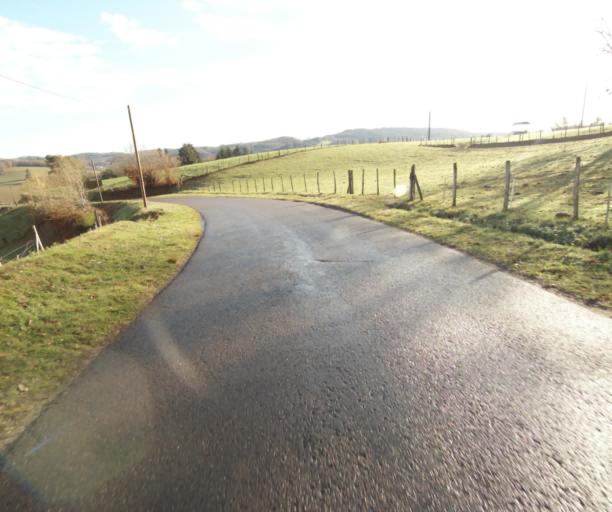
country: FR
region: Limousin
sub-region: Departement de la Correze
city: Saint-Mexant
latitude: 45.2418
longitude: 1.6332
